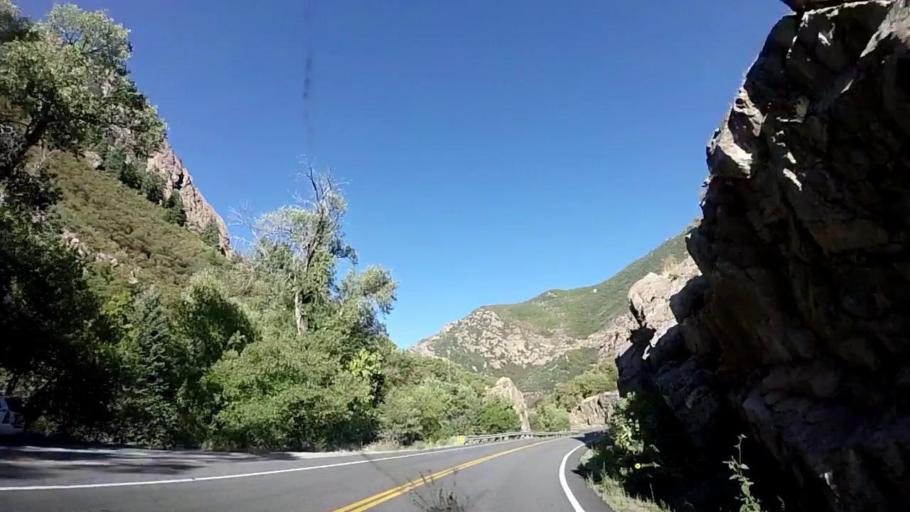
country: US
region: Utah
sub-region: Salt Lake County
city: Cottonwood Heights
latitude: 40.6231
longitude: -111.7596
